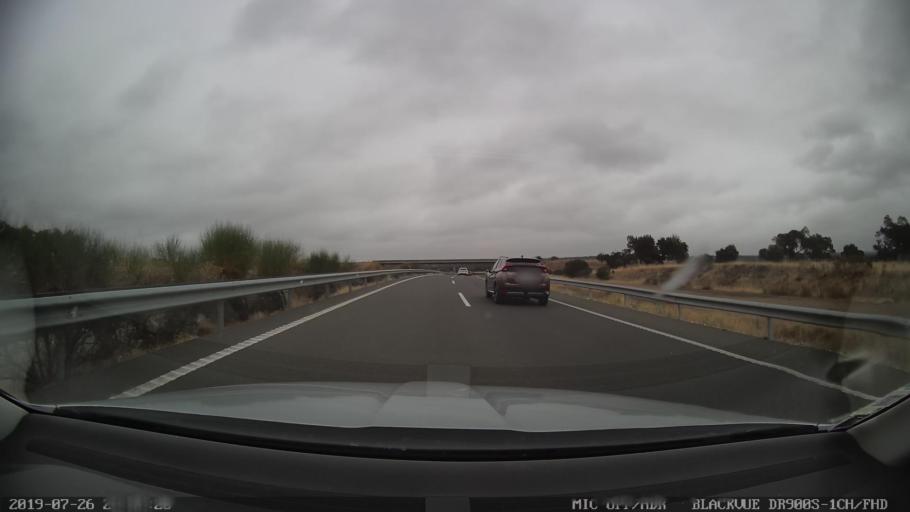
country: ES
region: Extremadura
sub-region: Provincia de Caceres
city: Jaraicejo
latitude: 39.6064
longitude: -5.8390
